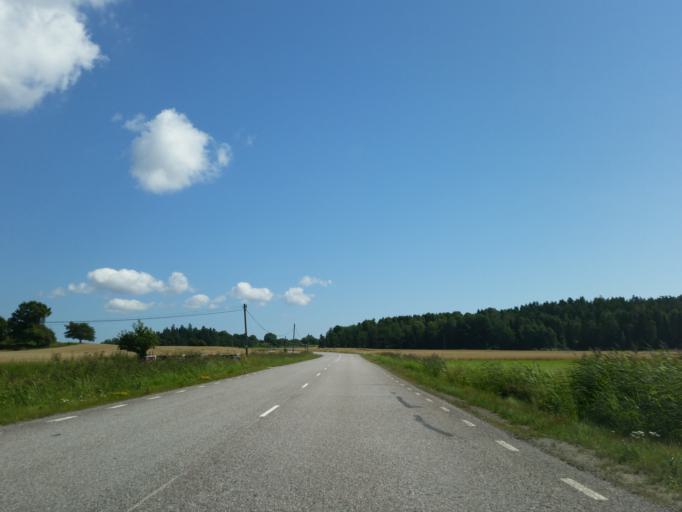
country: SE
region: Soedermanland
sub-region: Trosa Kommun
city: Vagnharad
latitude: 58.9875
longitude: 17.6279
